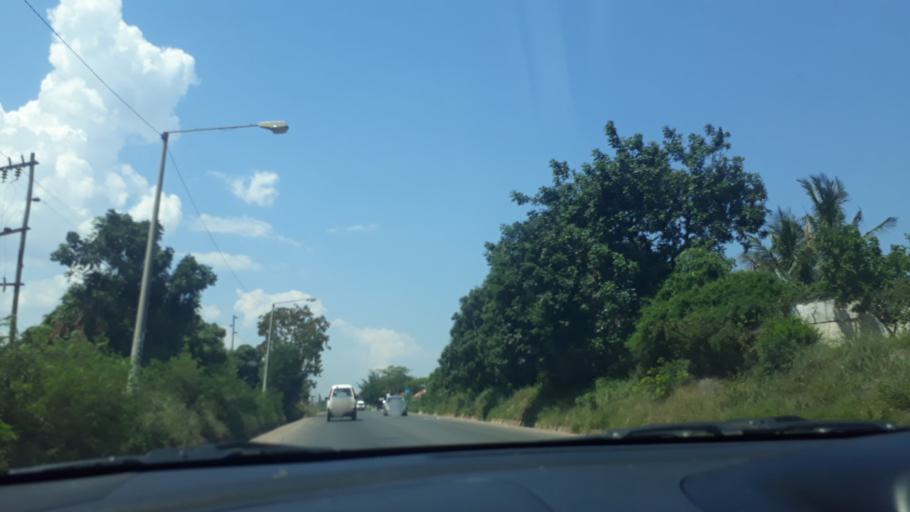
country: MZ
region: Maputo
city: Matola
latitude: -25.9610
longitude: 32.4493
